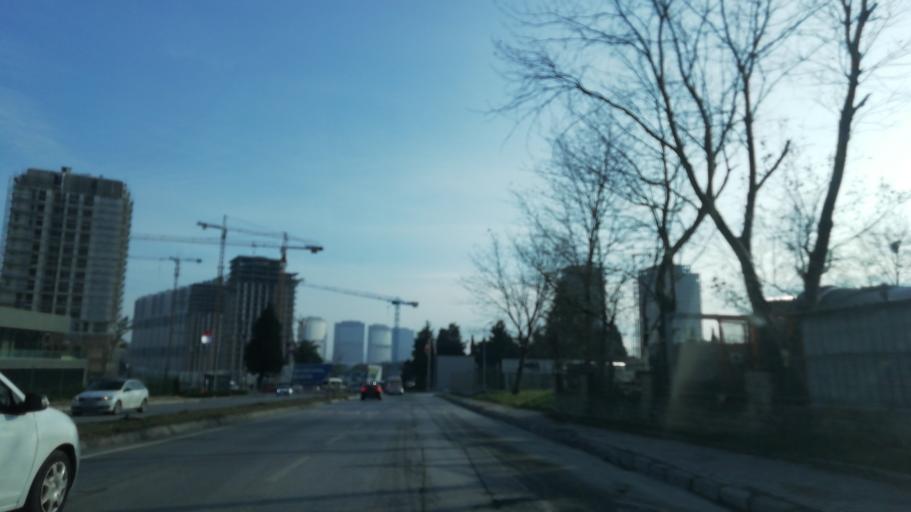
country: TR
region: Istanbul
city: Esenyurt
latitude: 41.0771
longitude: 28.6546
